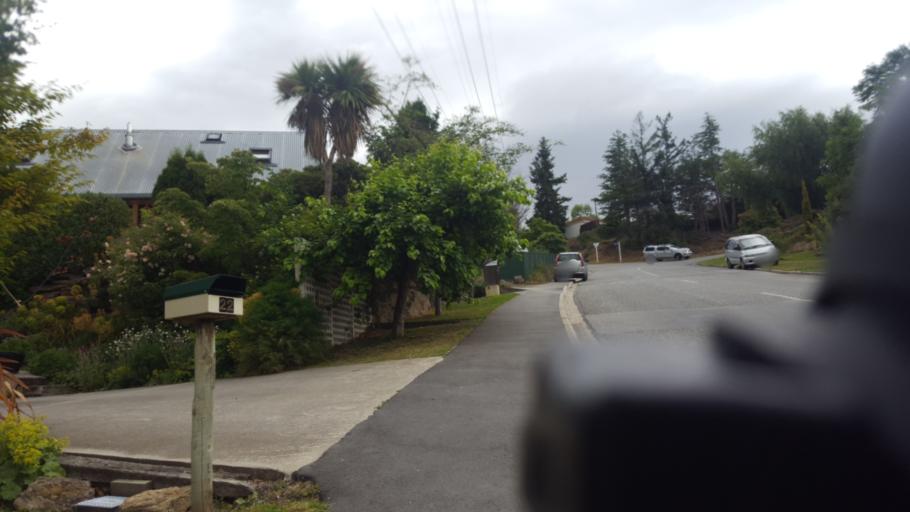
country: NZ
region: Otago
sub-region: Queenstown-Lakes District
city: Wanaka
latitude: -45.2604
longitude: 169.3834
